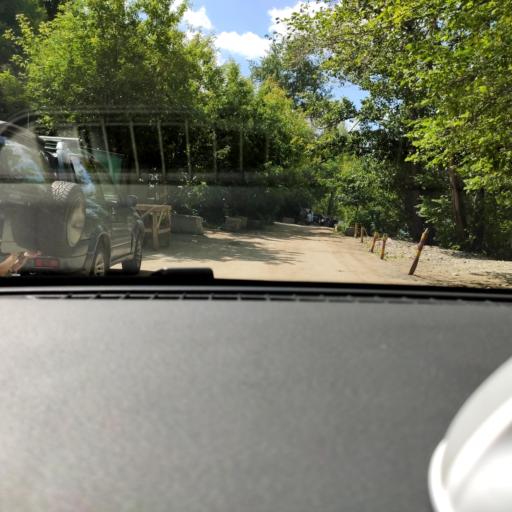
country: RU
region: Samara
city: Samara
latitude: 53.2248
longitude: 50.1481
